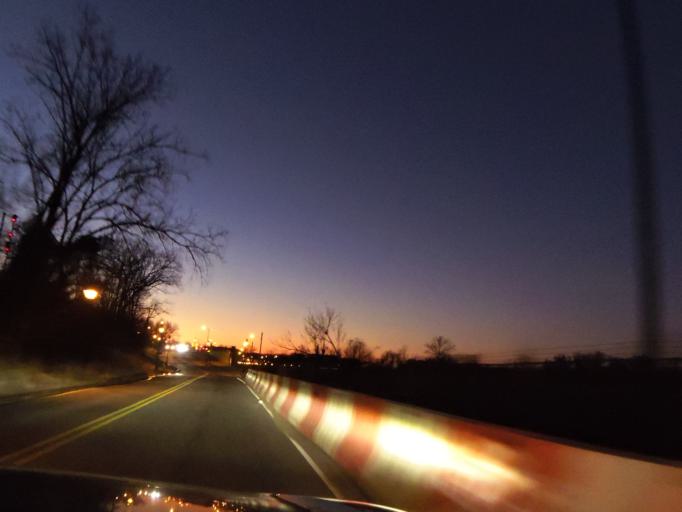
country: US
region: Virginia
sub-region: Henrico County
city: Montrose
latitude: 37.5261
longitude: -77.4205
